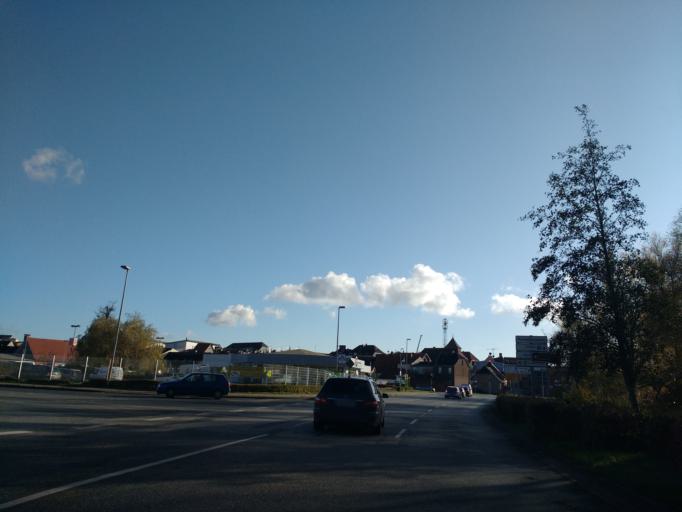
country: DE
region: Mecklenburg-Vorpommern
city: Grevesmuhlen
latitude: 53.8673
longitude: 11.1822
